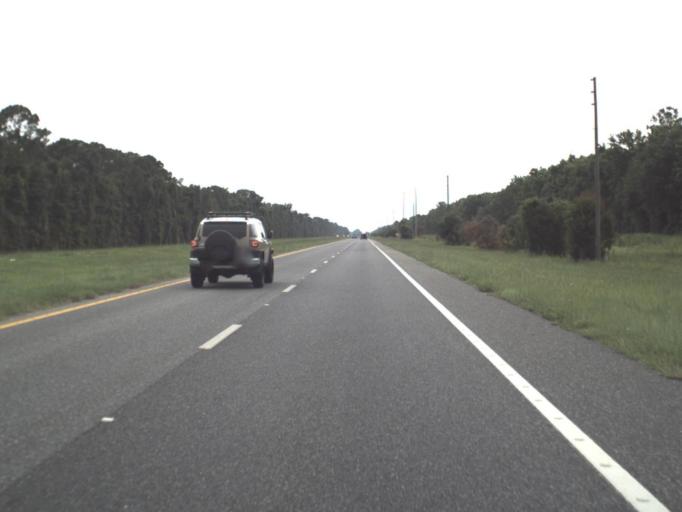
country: US
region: Florida
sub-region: Levy County
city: Inglis
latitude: 29.2196
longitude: -82.7026
